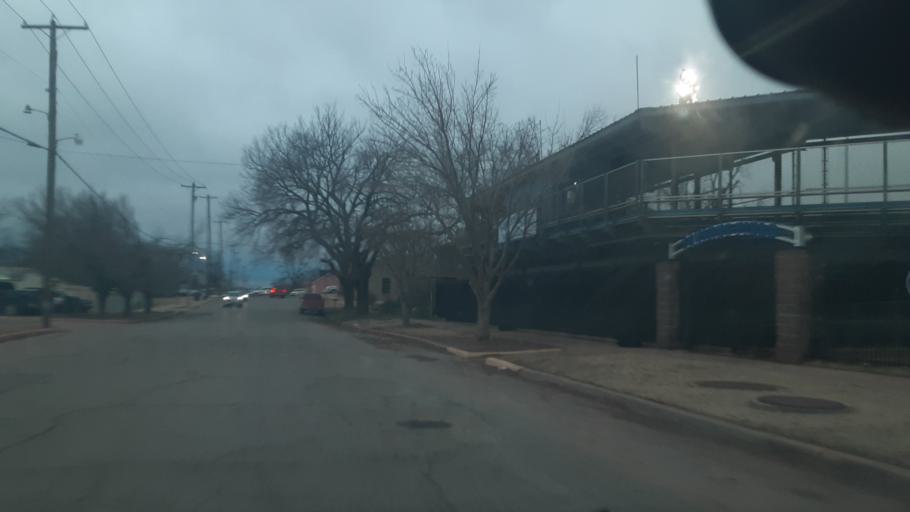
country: US
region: Oklahoma
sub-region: Logan County
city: Guthrie
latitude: 35.8749
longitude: -97.4239
